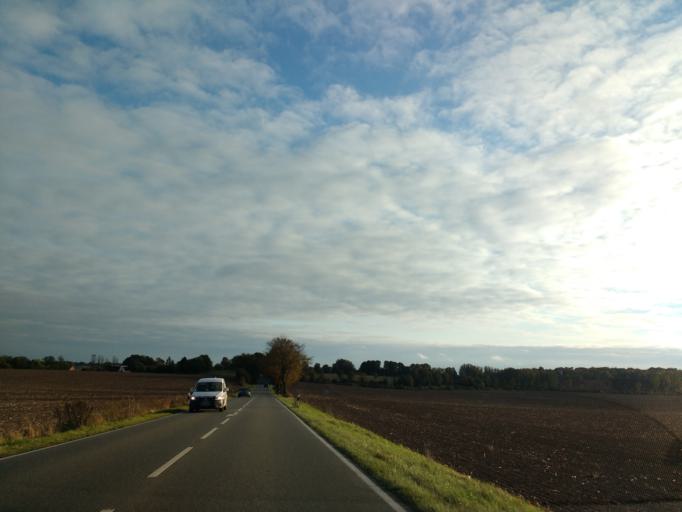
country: DE
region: Schleswig-Holstein
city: Altenkrempe
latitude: 54.1469
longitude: 10.8204
